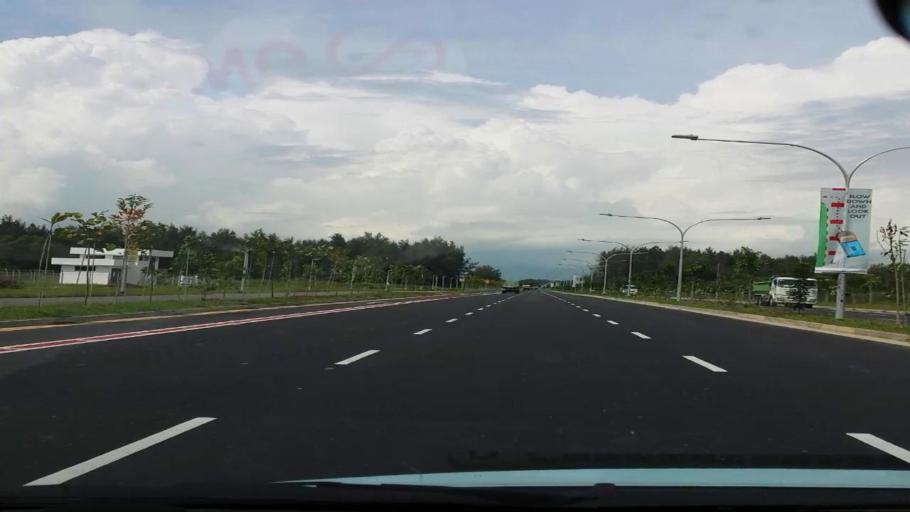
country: SG
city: Singapore
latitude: 1.3294
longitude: 104.0204
